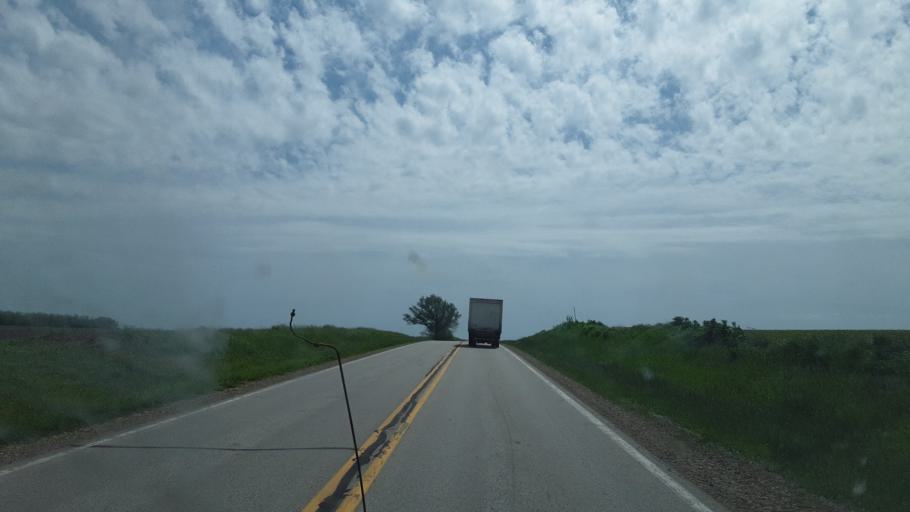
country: US
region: Illinois
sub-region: Logan County
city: Atlanta
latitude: 40.3112
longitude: -89.2213
